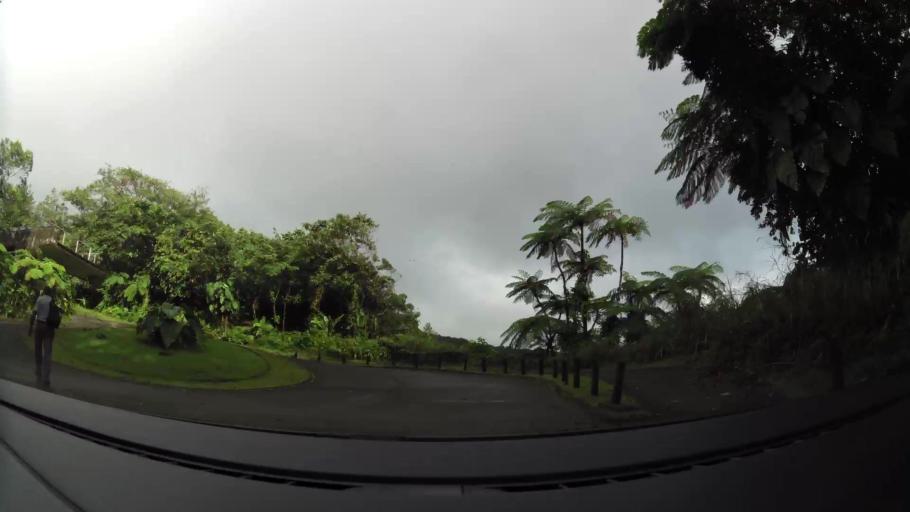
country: GP
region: Guadeloupe
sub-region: Guadeloupe
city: Saint-Claude
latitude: 16.0419
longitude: -61.6380
